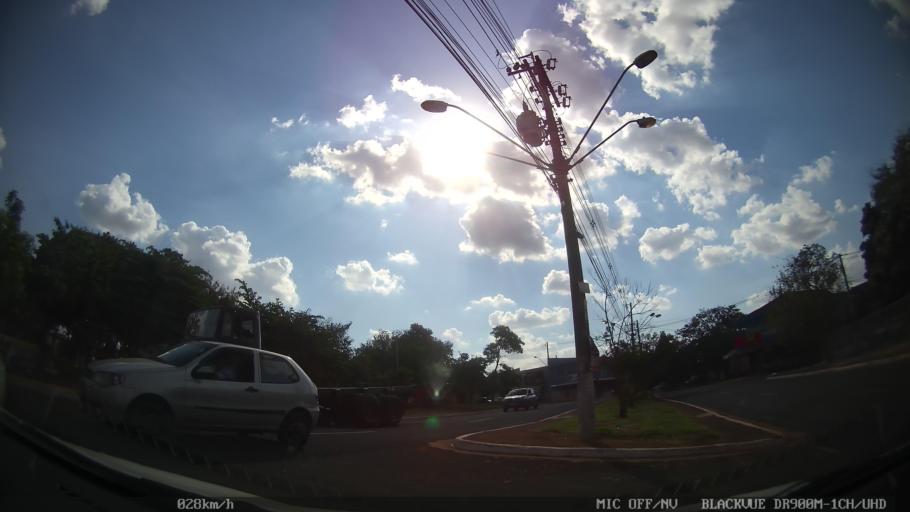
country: BR
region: Sao Paulo
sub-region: Ribeirao Preto
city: Ribeirao Preto
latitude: -21.1957
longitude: -47.8391
